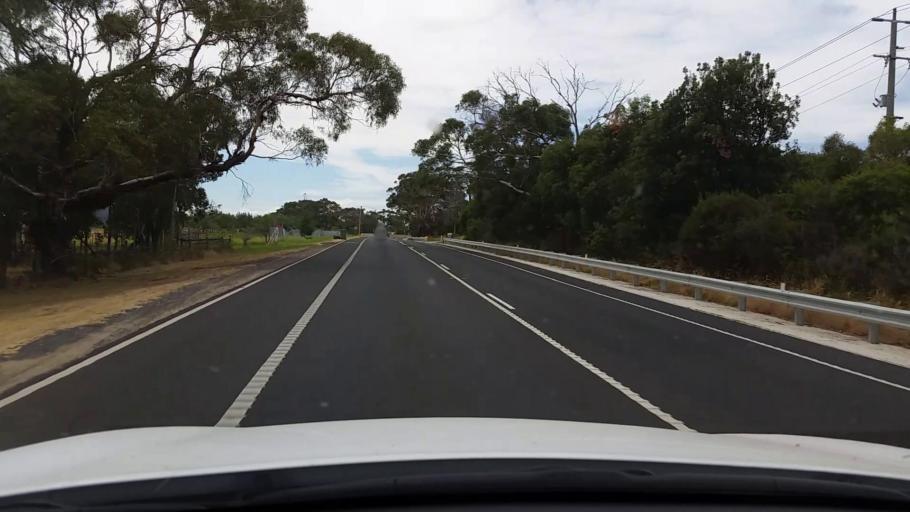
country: AU
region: Victoria
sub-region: Mornington Peninsula
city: Safety Beach
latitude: -38.3180
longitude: 145.0168
